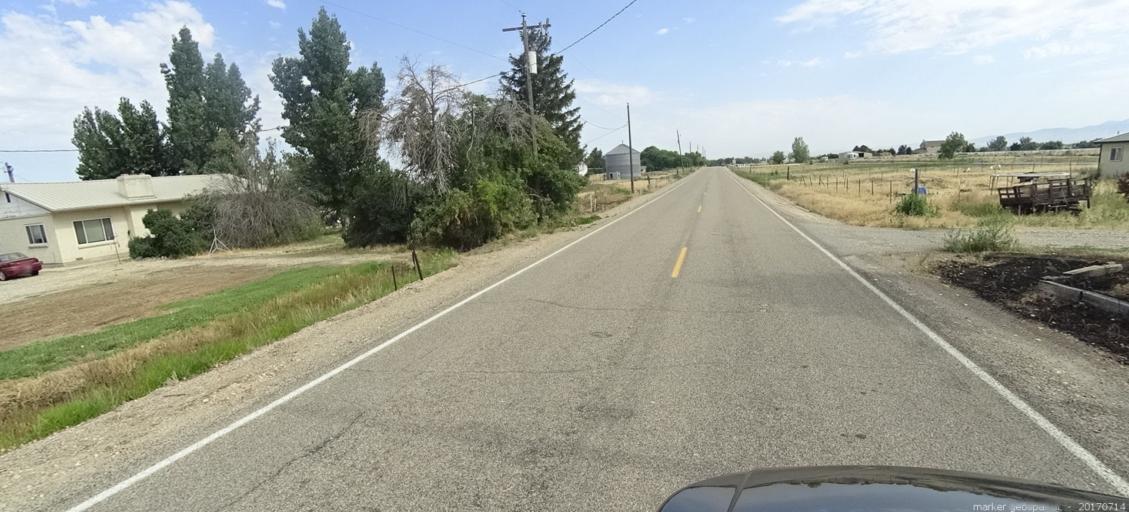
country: US
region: Idaho
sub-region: Ada County
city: Kuna
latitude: 43.4957
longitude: -116.3543
